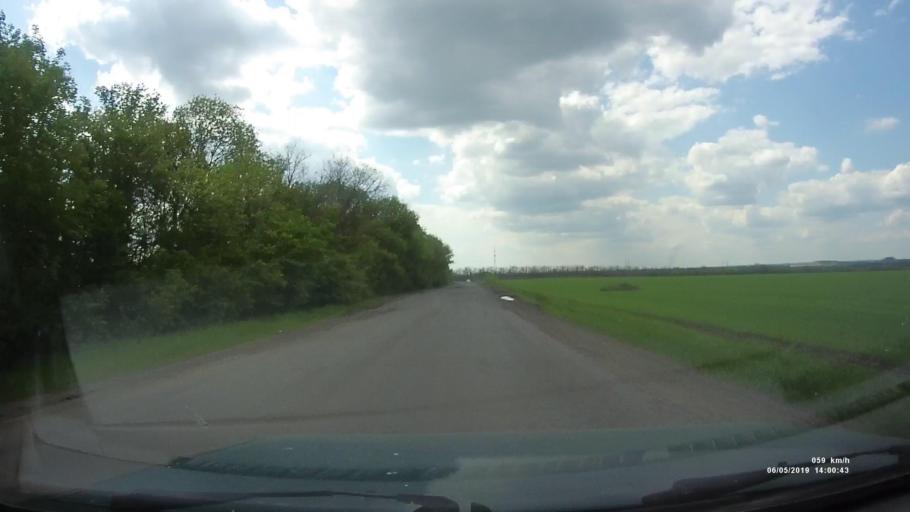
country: RU
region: Rostov
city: Shakhty
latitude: 47.6852
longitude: 40.3856
